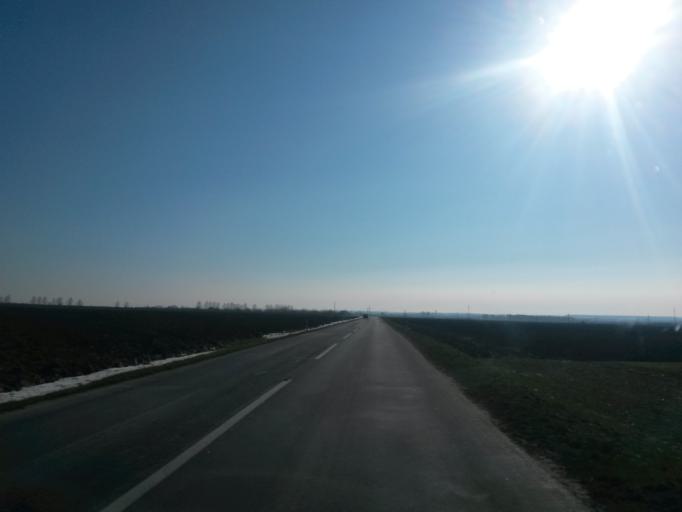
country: HR
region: Osjecko-Baranjska
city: Dalj
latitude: 45.5076
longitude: 18.9405
